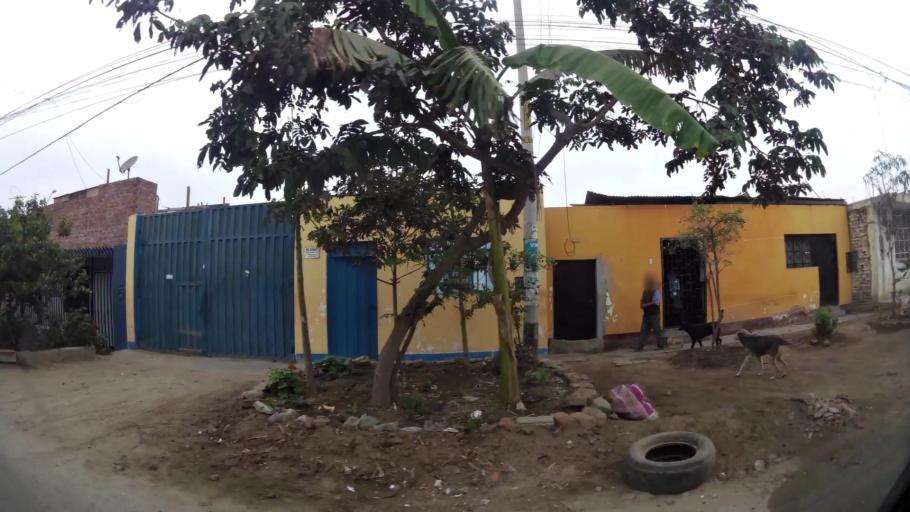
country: PE
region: La Libertad
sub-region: Provincia de Trujillo
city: La Esperanza
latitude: -8.0806
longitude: -79.0534
